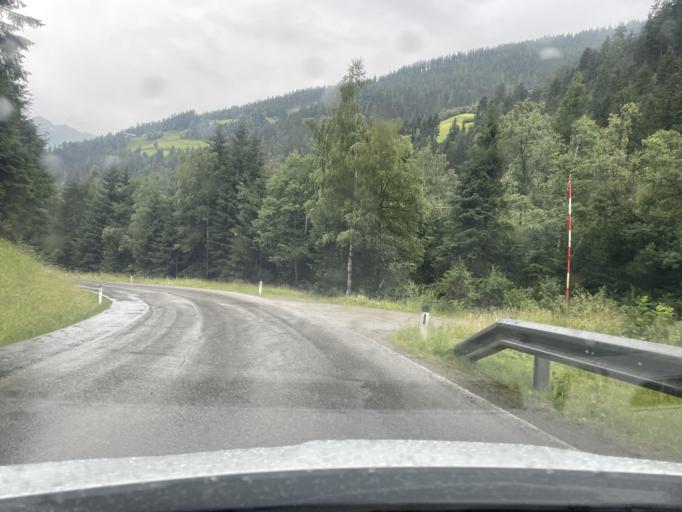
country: AT
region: Tyrol
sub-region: Politischer Bezirk Lienz
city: Ausservillgraten
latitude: 46.7707
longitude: 12.4287
